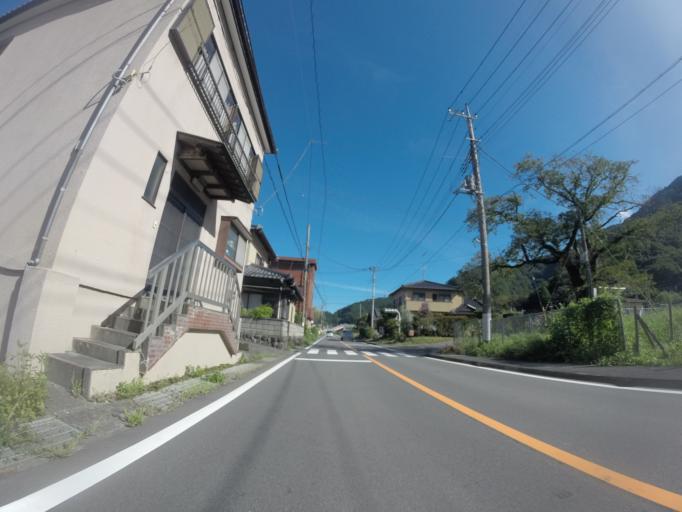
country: JP
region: Shizuoka
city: Fujinomiya
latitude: 35.3277
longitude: 138.4517
